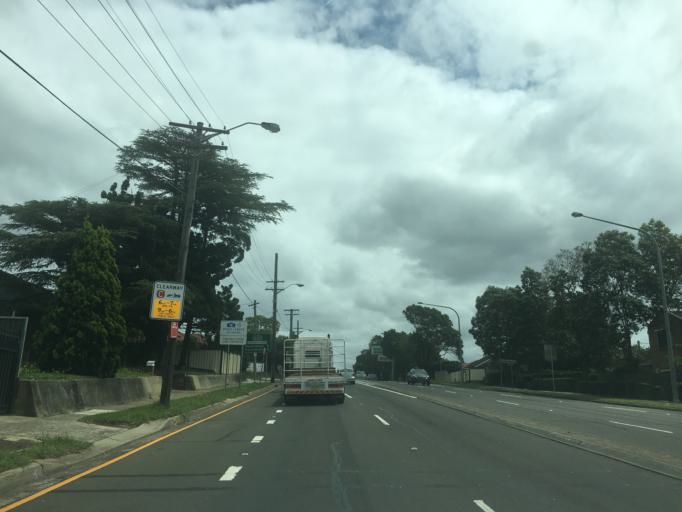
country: AU
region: New South Wales
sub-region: Parramatta
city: Ermington
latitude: -33.8137
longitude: 151.0511
